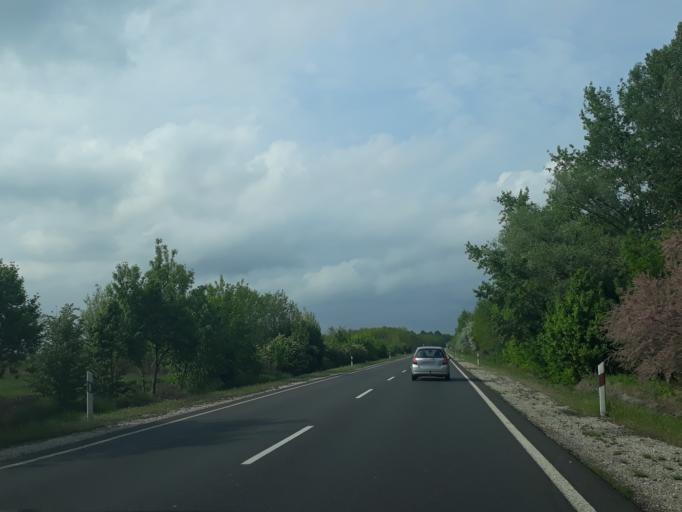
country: HU
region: Szabolcs-Szatmar-Bereg
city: Nyirtass
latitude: 48.0929
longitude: 21.9872
